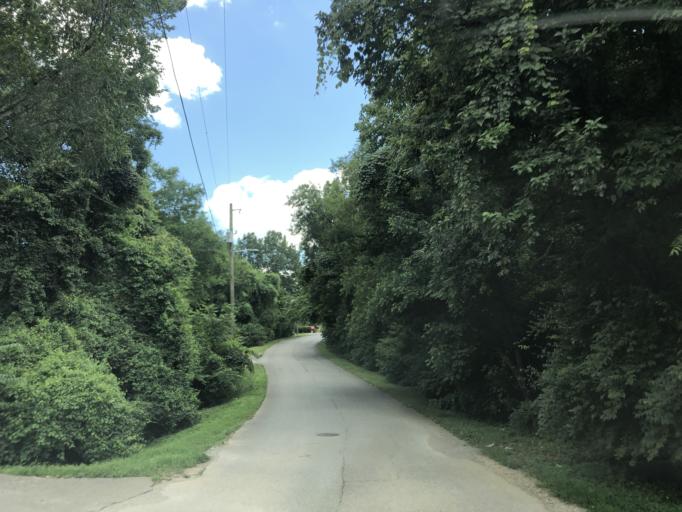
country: US
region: Tennessee
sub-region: Davidson County
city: Oak Hill
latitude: 36.0747
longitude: -86.7203
